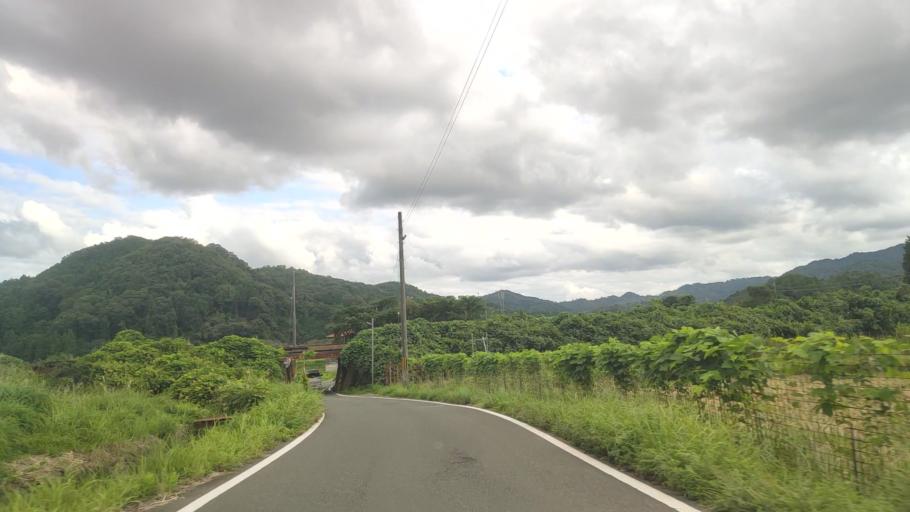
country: JP
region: Hyogo
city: Toyooka
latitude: 35.5980
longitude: 134.8843
